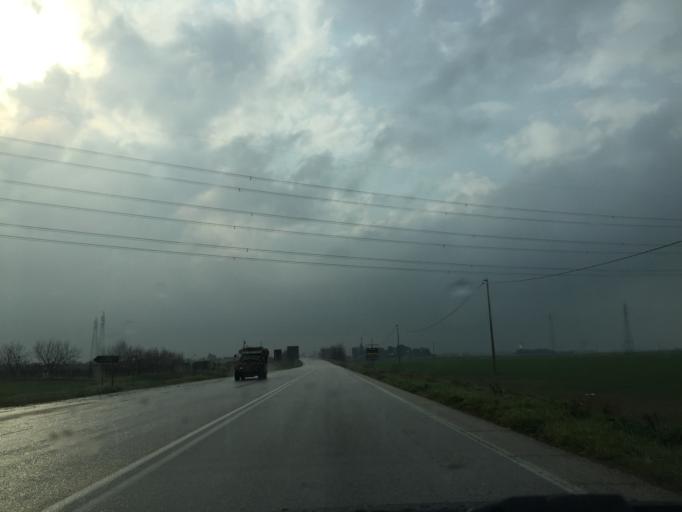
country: IT
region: Apulia
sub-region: Provincia di Foggia
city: Foggia
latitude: 41.4962
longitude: 15.5202
